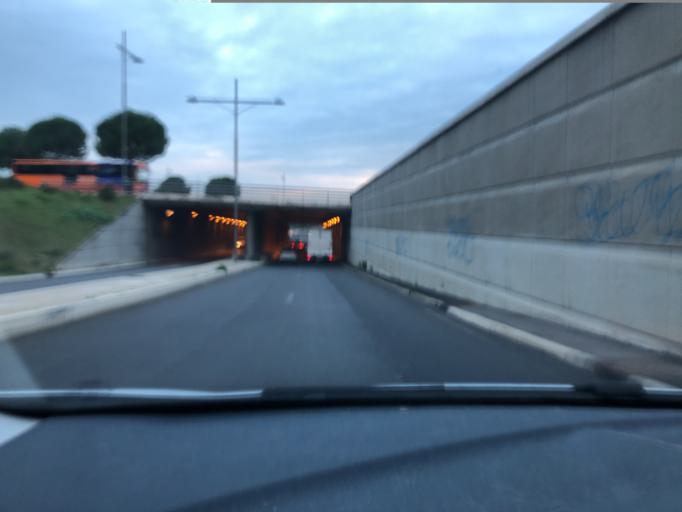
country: FR
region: Languedoc-Roussillon
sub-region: Departement de l'Herault
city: Montferrier-sur-Lez
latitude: 43.6419
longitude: 3.8474
